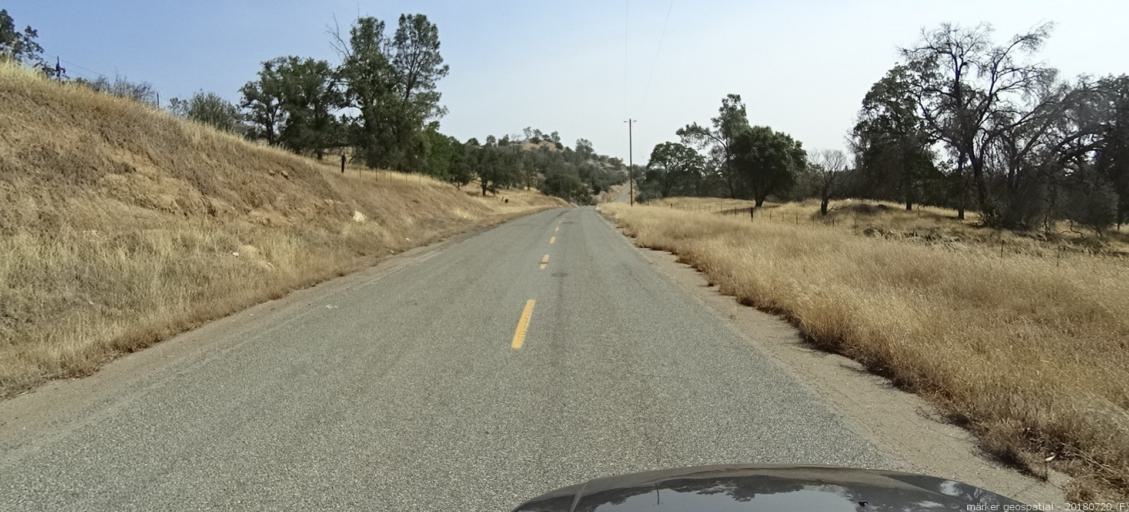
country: US
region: California
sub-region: Madera County
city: Yosemite Lakes
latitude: 37.2591
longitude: -119.8654
